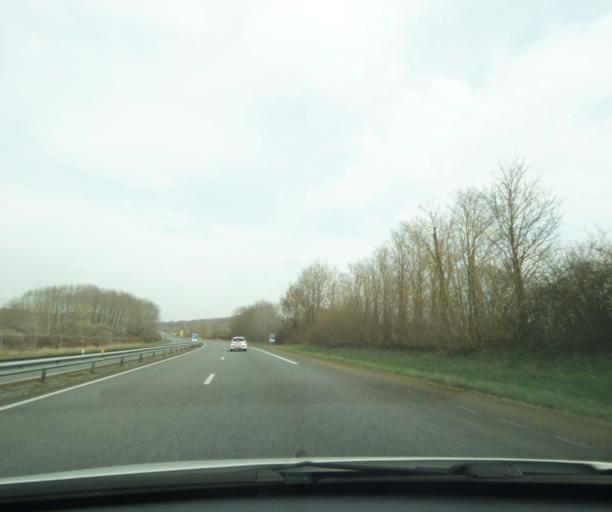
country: FR
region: Aquitaine
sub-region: Departement des Landes
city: Labatut
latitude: 43.5072
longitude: -1.0170
